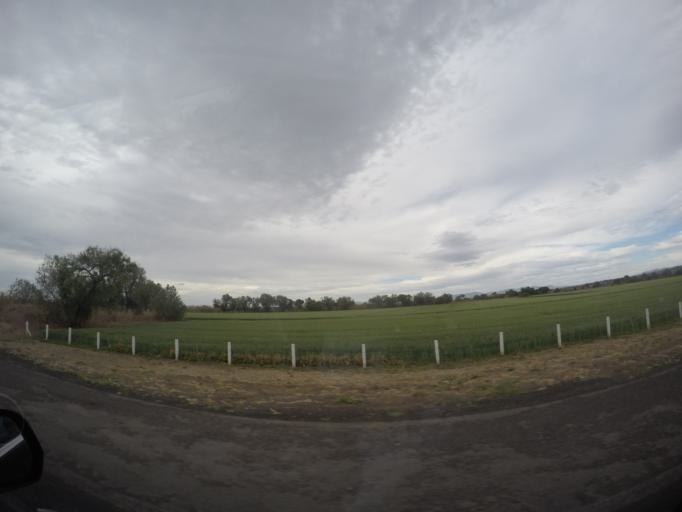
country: MX
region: Guanajuato
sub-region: Irapuato
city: Serrano
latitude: 20.7793
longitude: -101.4088
